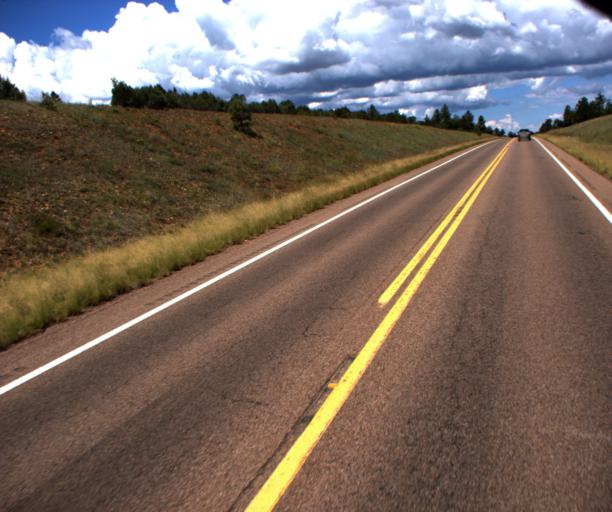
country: US
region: Arizona
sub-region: Navajo County
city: Heber-Overgaard
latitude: 34.3741
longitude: -110.4610
